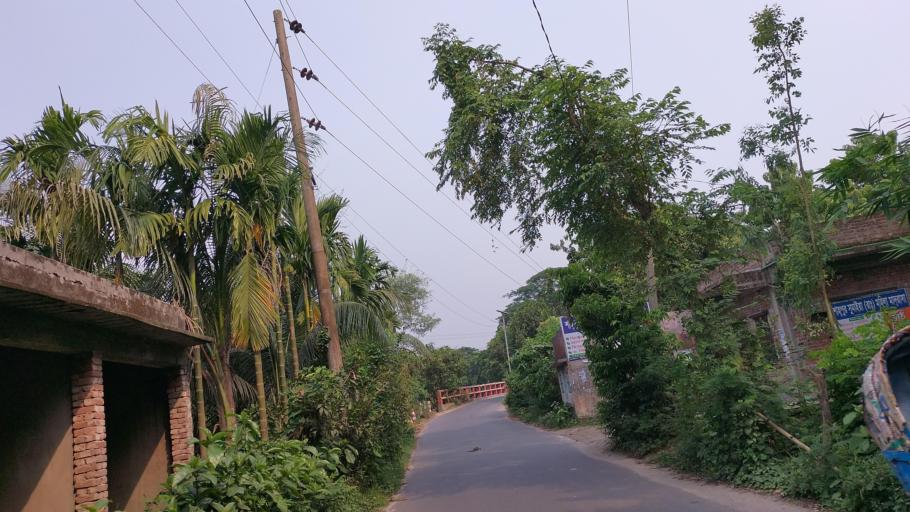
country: BD
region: Dhaka
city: Azimpur
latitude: 23.6764
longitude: 90.3174
